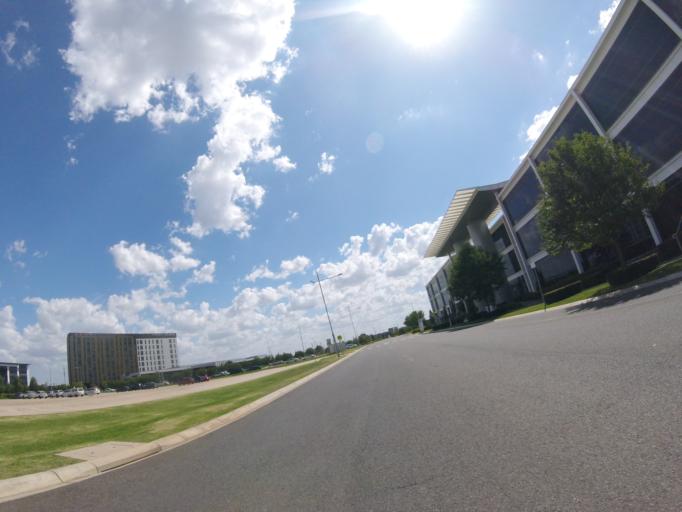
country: AU
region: Victoria
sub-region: Moonee Valley
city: Airport West
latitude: -37.7237
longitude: 144.8945
